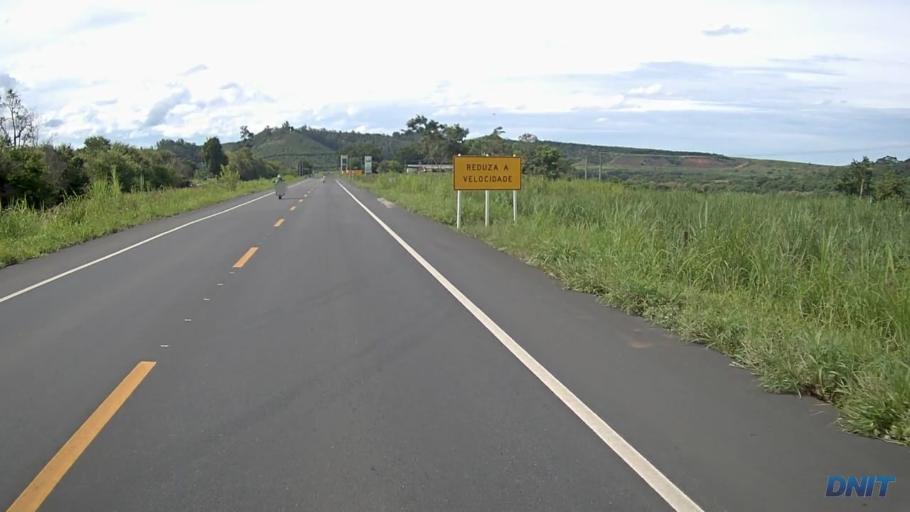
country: BR
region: Minas Gerais
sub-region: Ipaba
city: Ipaba
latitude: -19.2888
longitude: -42.3562
